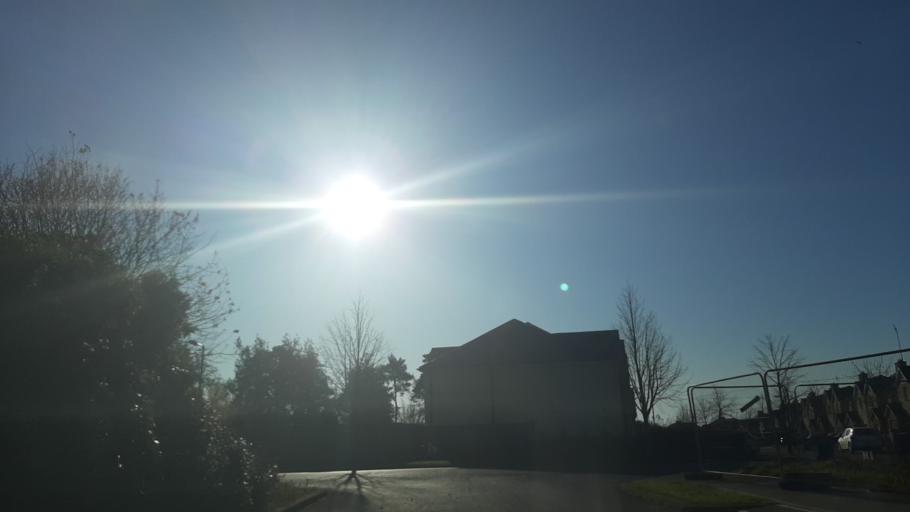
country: IE
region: Leinster
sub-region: Kildare
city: Rathangan
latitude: 53.2200
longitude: -7.0063
